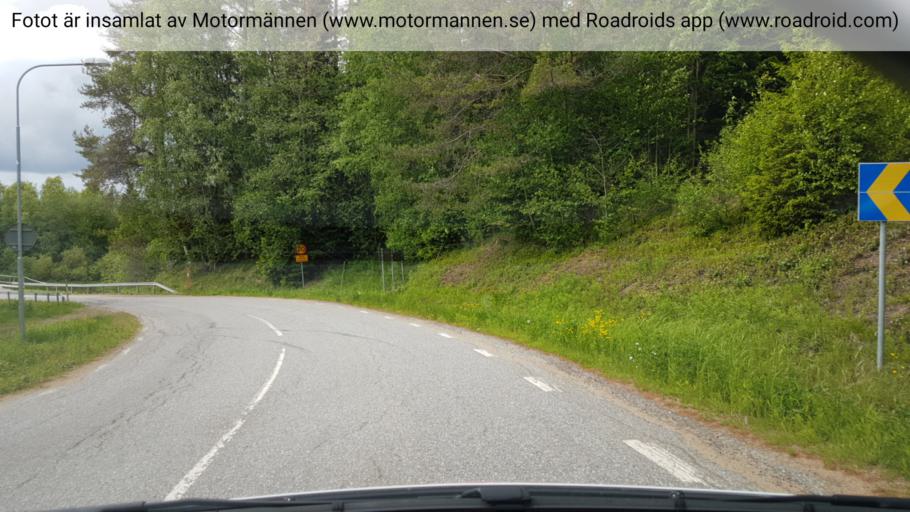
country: SE
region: Vaesterbotten
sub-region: Nordmalings Kommun
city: Nordmaling
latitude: 63.5632
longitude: 19.6989
